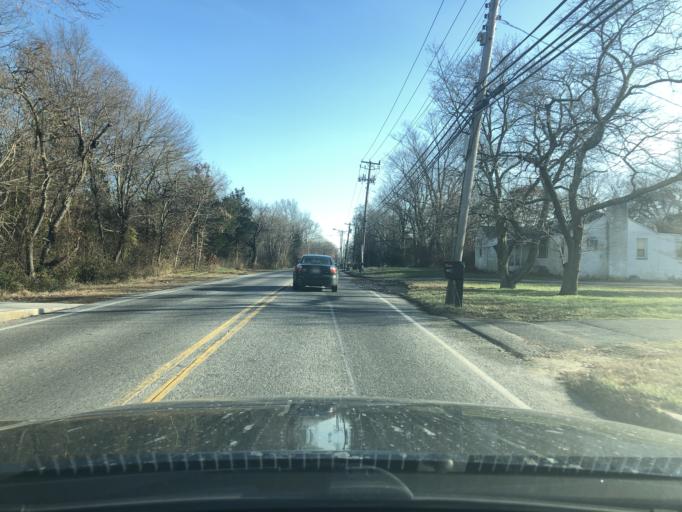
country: US
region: New Jersey
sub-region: Atlantic County
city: Northfield
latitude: 39.3906
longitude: -74.5501
